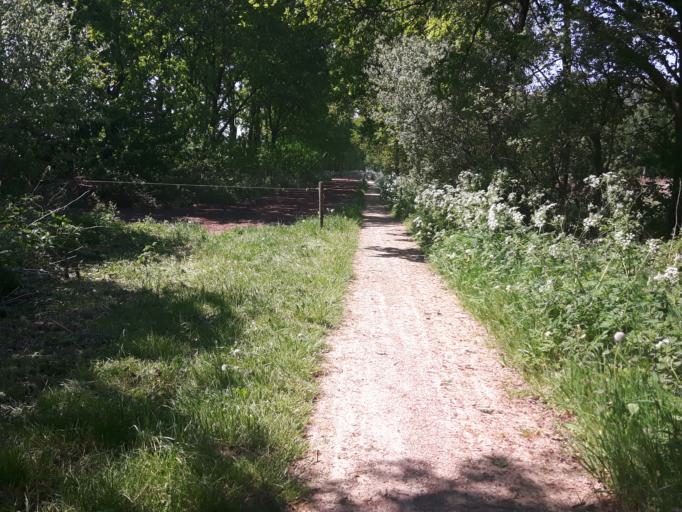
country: NL
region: Overijssel
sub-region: Gemeente Enschede
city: Enschede
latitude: 52.1532
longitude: 6.8610
